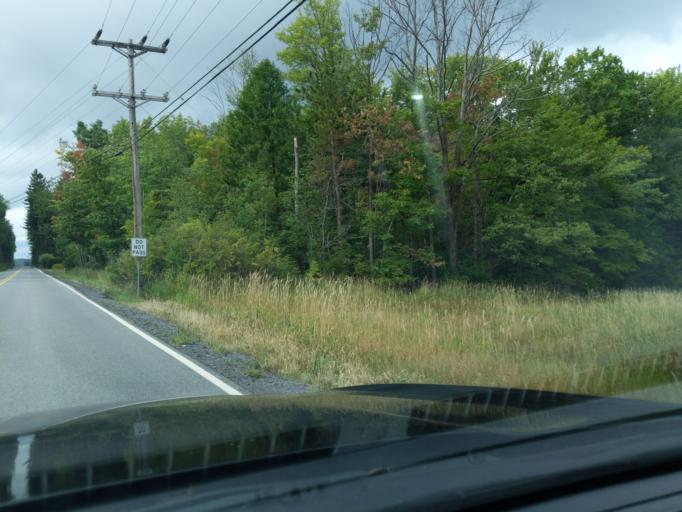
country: US
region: Pennsylvania
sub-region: Blair County
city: Claysburg
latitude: 40.3259
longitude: -78.5660
